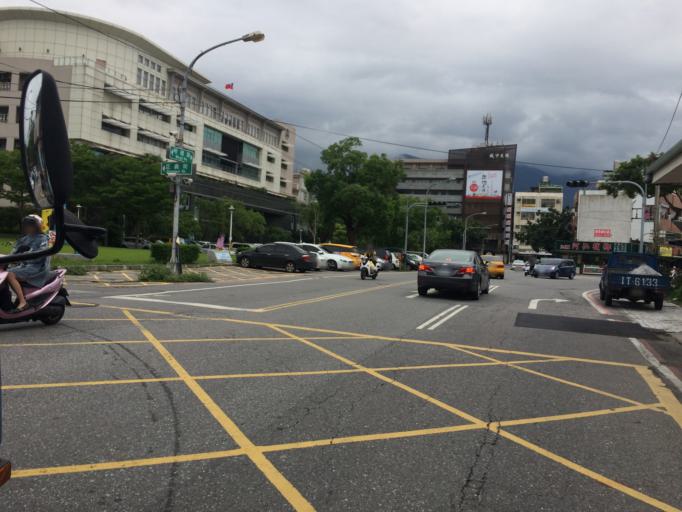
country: TW
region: Taiwan
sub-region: Hualien
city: Hualian
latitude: 23.9840
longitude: 121.6072
